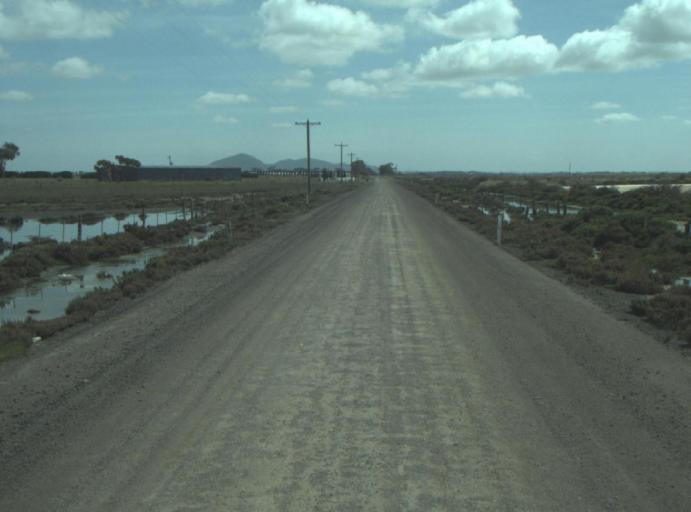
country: AU
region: Victoria
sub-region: Greater Geelong
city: Lara
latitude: -38.0821
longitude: 144.4228
